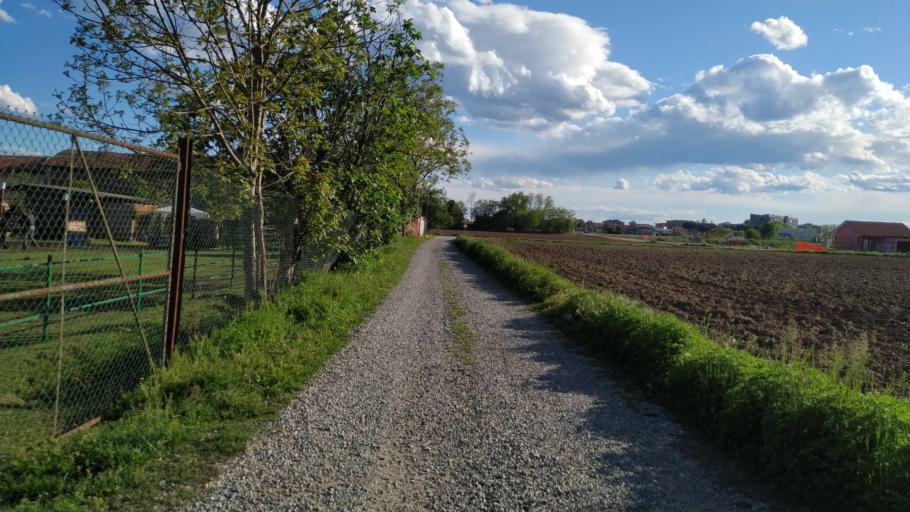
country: IT
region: Piedmont
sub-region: Provincia di Vercelli
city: Santhia
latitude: 45.3752
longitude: 8.1695
